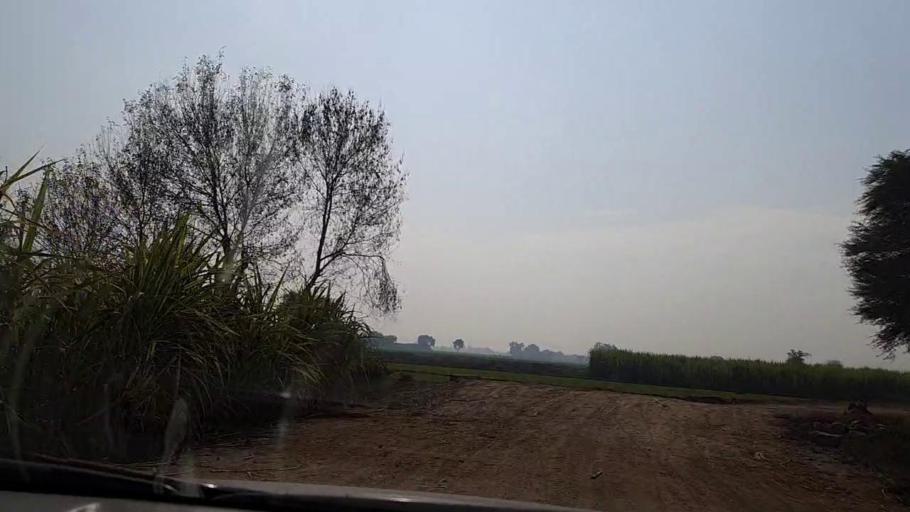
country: PK
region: Sindh
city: Daulatpur
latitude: 26.5399
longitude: 67.9879
